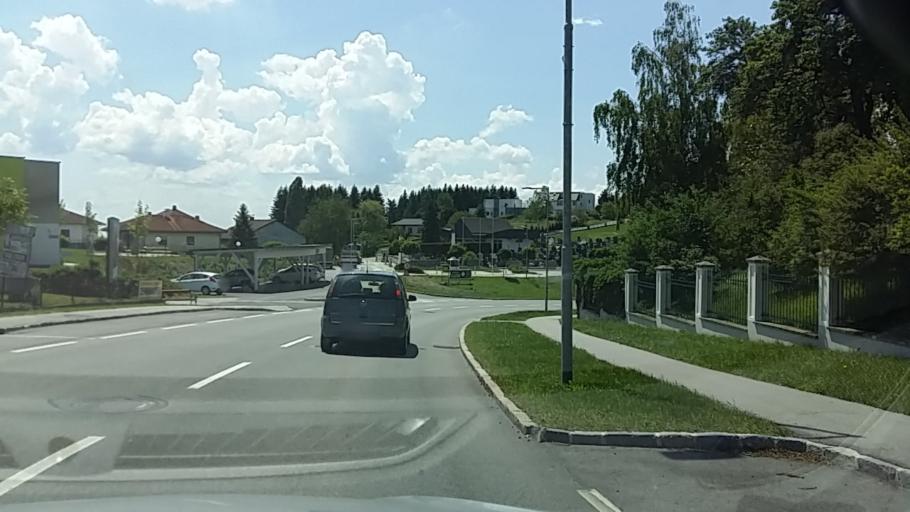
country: AT
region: Burgenland
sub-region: Politischer Bezirk Oberwart
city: Bernstein
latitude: 47.4042
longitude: 16.2559
